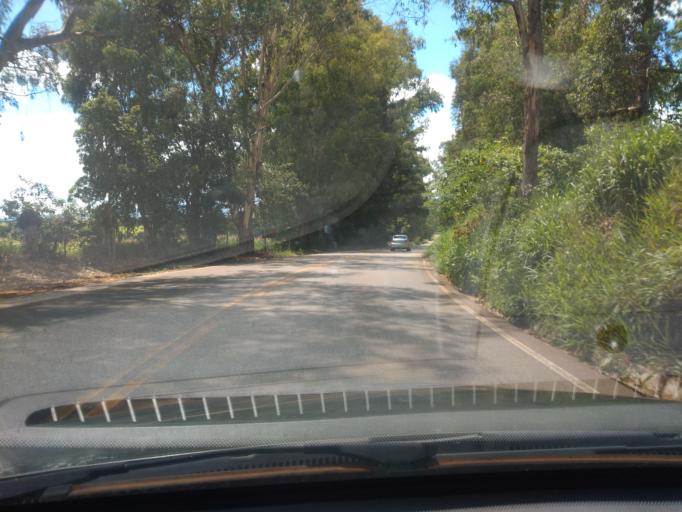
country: BR
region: Minas Gerais
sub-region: Tres Coracoes
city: Tres Coracoes
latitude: -21.6503
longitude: -45.1084
